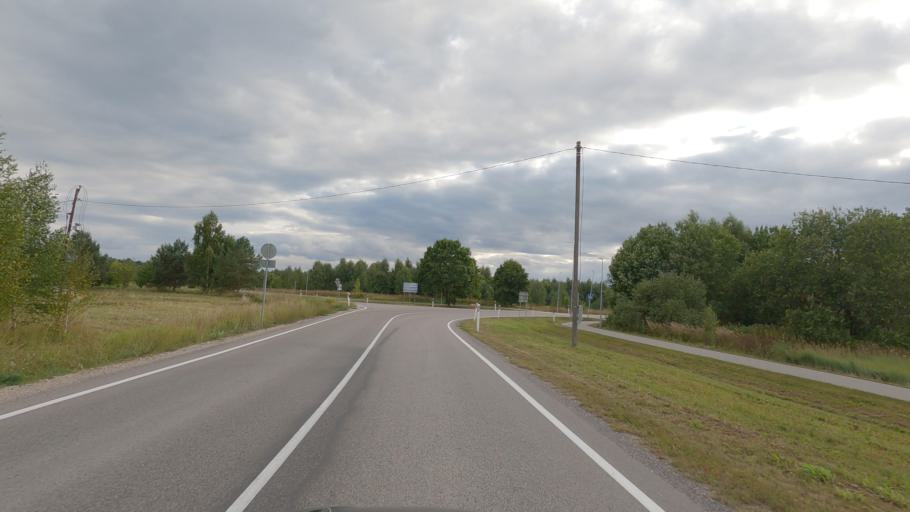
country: EE
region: Raplamaa
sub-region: Kohila vald
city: Kohila
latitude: 59.1769
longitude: 24.7687
